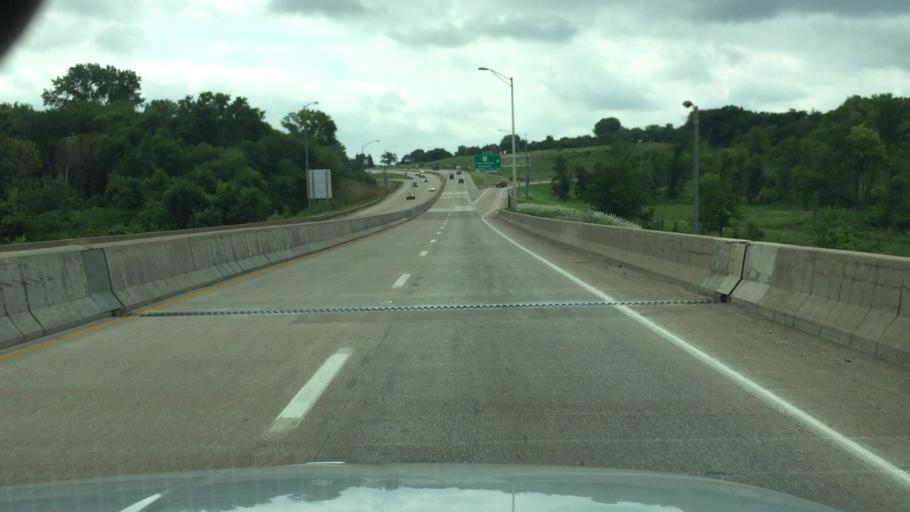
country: US
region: Iowa
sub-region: Scott County
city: Le Claire
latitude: 41.5764
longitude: -90.3628
